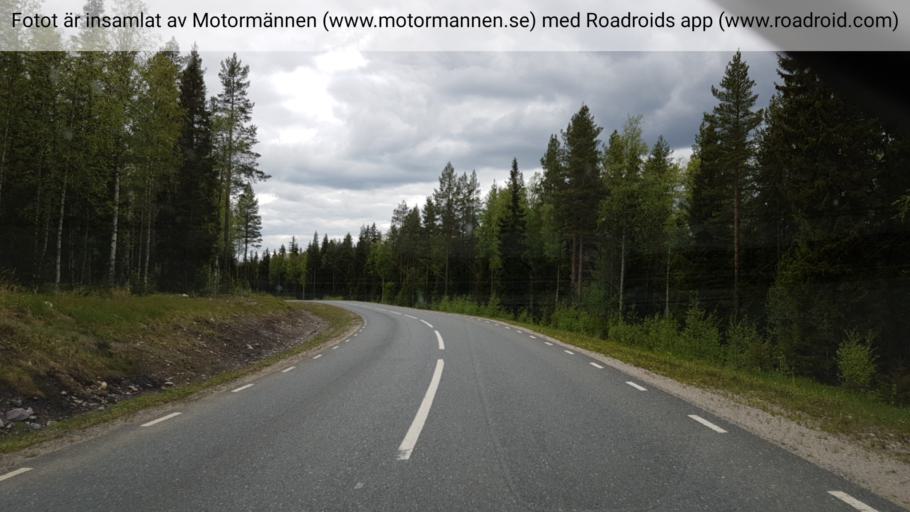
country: SE
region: Vaesterbotten
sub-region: Vindelns Kommun
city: Vindeln
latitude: 64.4811
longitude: 19.7694
